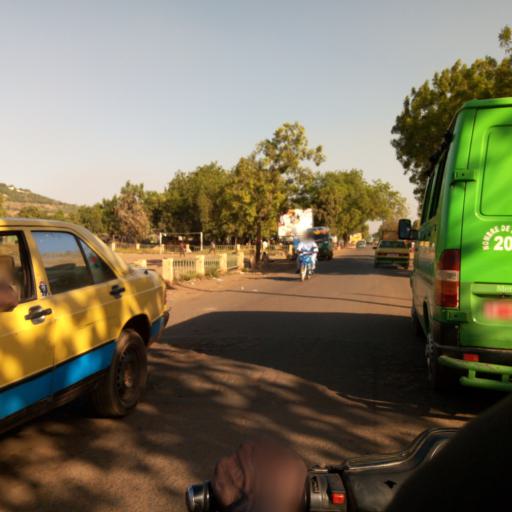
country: ML
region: Bamako
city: Bamako
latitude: 12.6544
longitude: -8.0218
